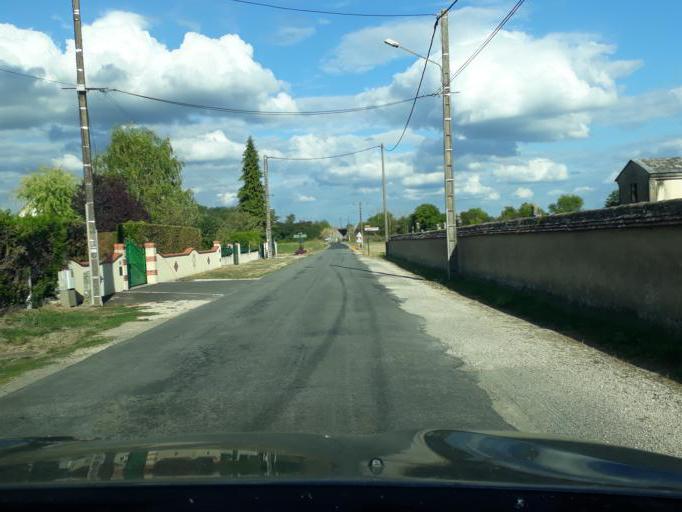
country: FR
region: Centre
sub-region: Departement du Loiret
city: Rebrechien
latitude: 47.9877
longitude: 2.0478
